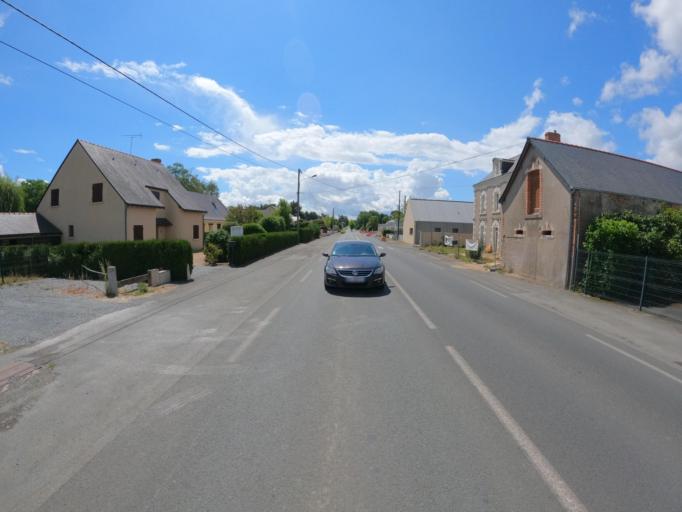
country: FR
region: Pays de la Loire
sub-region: Departement de Maine-et-Loire
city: Champigne
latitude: 47.6612
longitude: -0.5736
